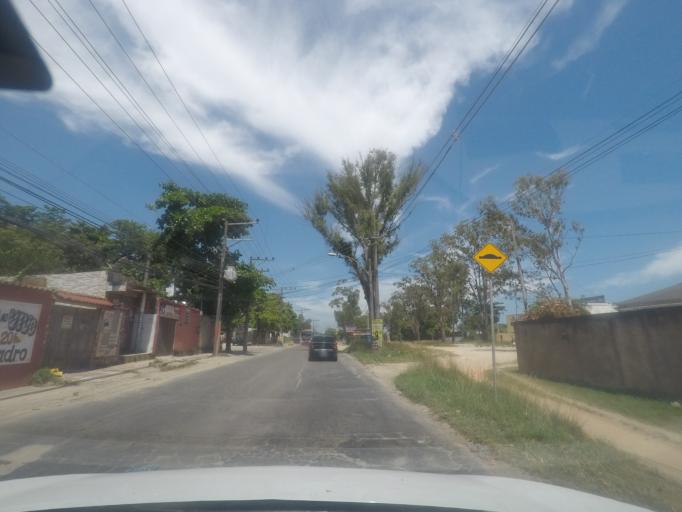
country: BR
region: Rio de Janeiro
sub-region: Itaguai
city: Itaguai
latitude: -22.9778
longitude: -43.6724
